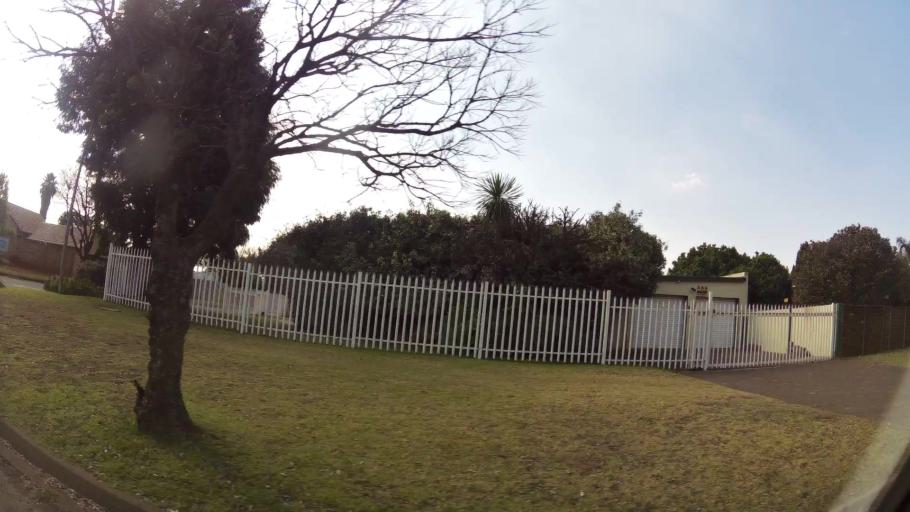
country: ZA
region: Gauteng
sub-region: Ekurhuleni Metropolitan Municipality
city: Boksburg
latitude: -26.1901
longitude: 28.2356
